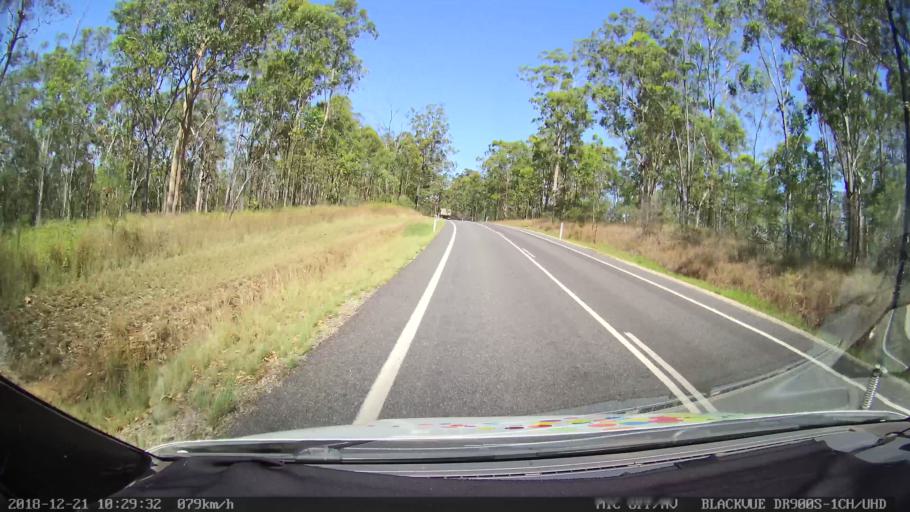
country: AU
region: New South Wales
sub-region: Clarence Valley
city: South Grafton
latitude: -29.6321
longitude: 152.7206
